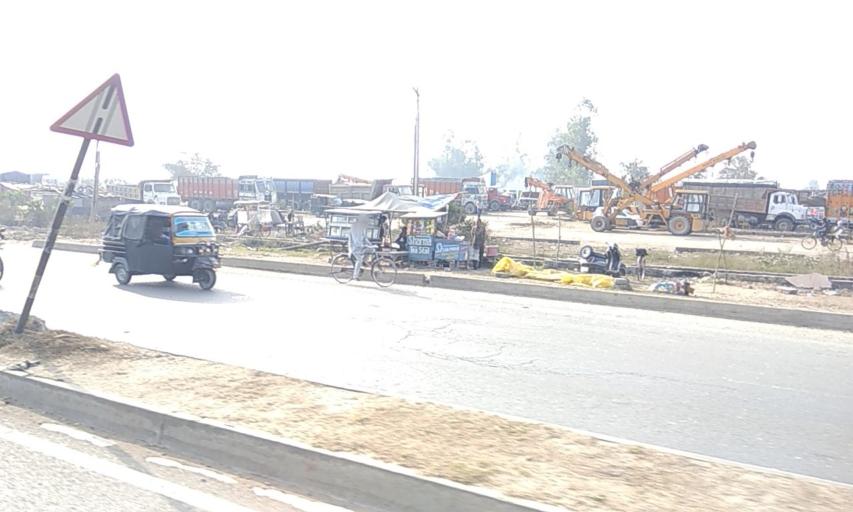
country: IN
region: Punjab
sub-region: Pathankot
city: Pathankot
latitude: 32.2575
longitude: 75.6362
